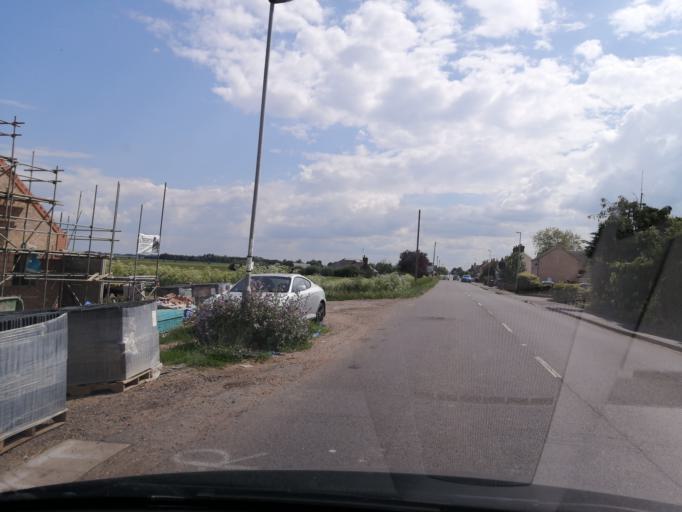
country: GB
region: England
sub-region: Cambridgeshire
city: Ramsey
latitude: 52.4781
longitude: -0.1515
